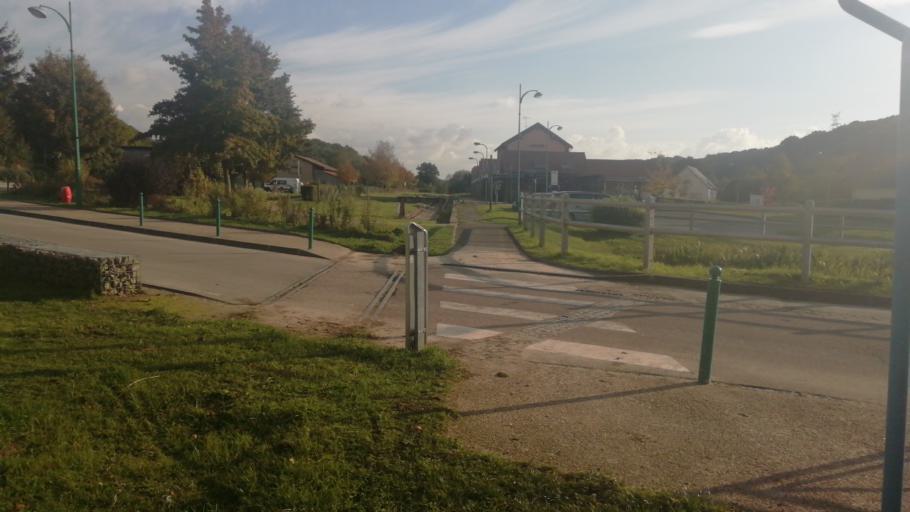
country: FR
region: Haute-Normandie
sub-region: Departement de la Seine-Maritime
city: Rolleville
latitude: 49.5825
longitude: 0.2157
